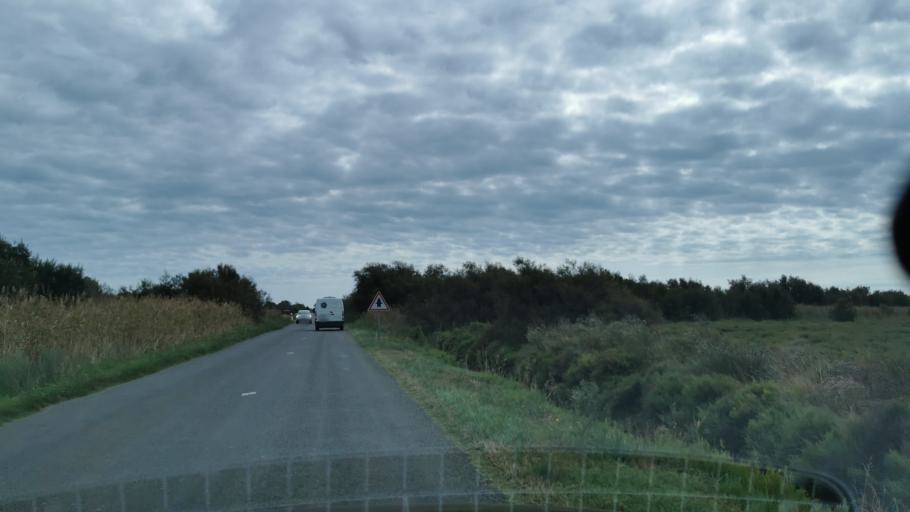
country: FR
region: Languedoc-Roussillon
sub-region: Departement de l'Herault
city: Vendres
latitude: 43.2264
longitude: 3.2091
